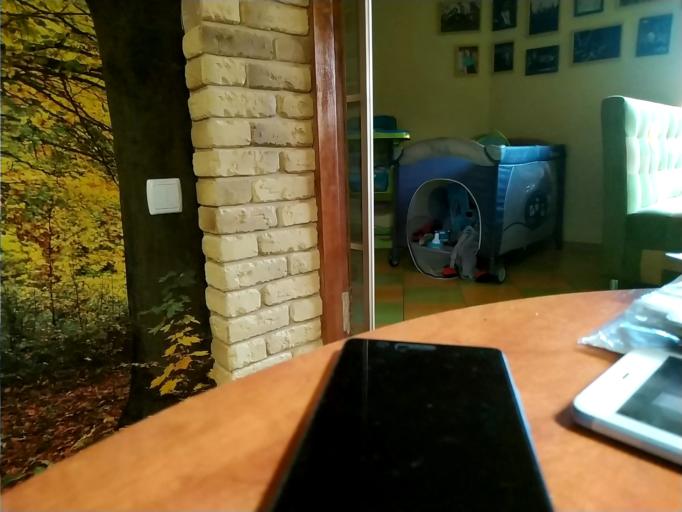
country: RU
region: Kaluga
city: Seredeyskiy
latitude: 53.7529
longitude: 35.4113
